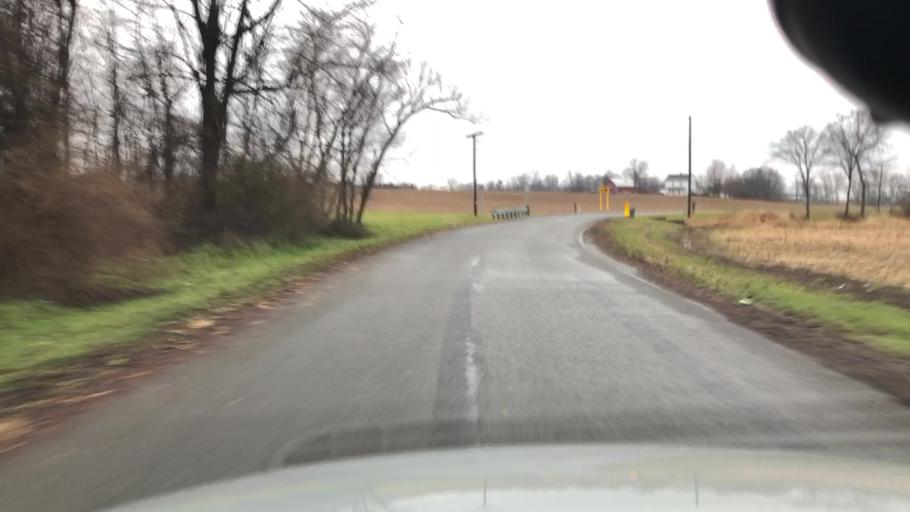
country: US
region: Ohio
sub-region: Allen County
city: Lima
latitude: 40.7388
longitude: -83.9935
